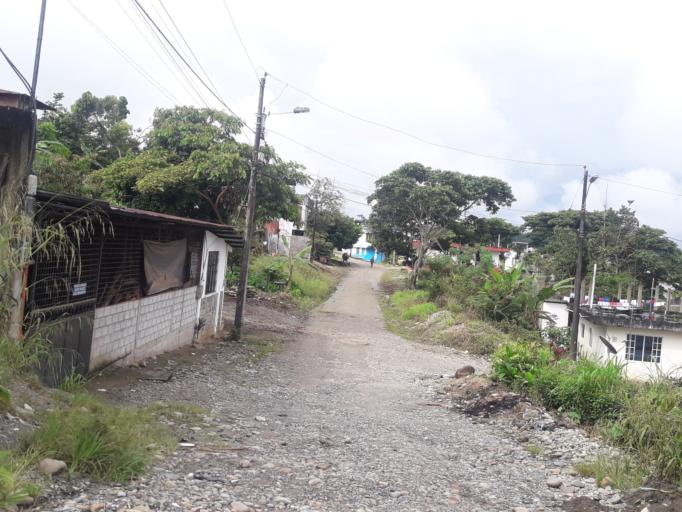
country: EC
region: Napo
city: Tena
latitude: -0.9963
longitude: -77.8077
